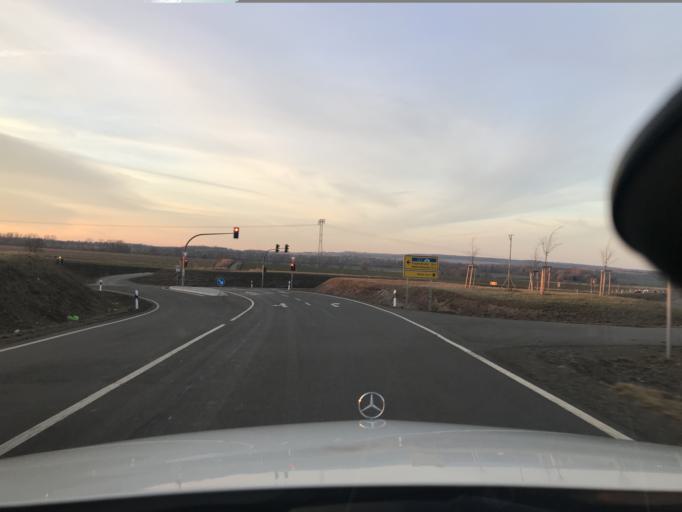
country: DE
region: Thuringia
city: Emleben
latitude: 50.9150
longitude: 10.6513
